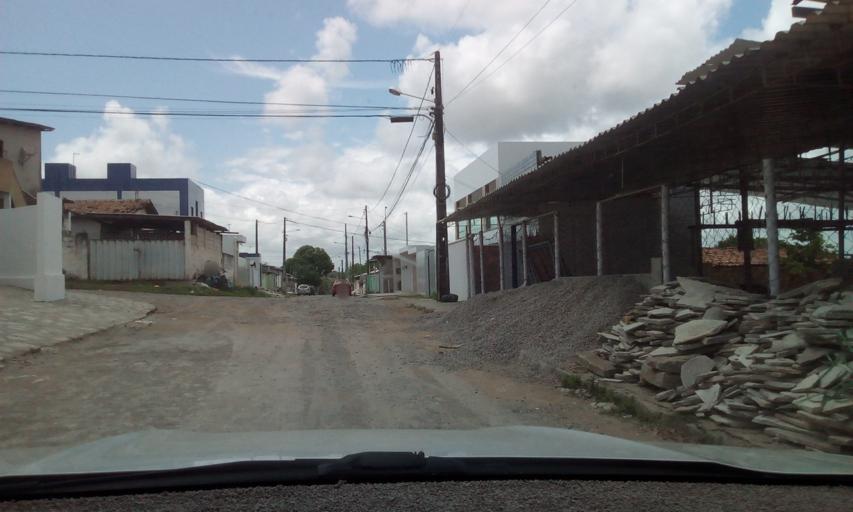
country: BR
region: Paraiba
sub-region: Joao Pessoa
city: Joao Pessoa
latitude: -7.1875
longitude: -34.8415
